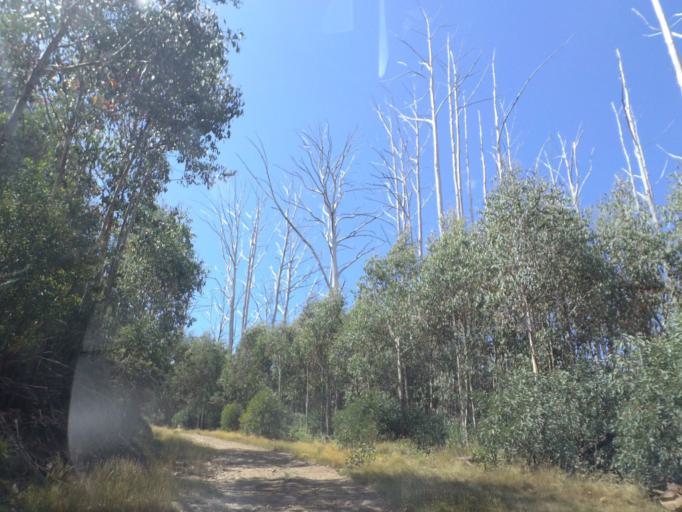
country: AU
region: Victoria
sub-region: Murrindindi
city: Alexandra
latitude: -37.4629
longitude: 145.8364
